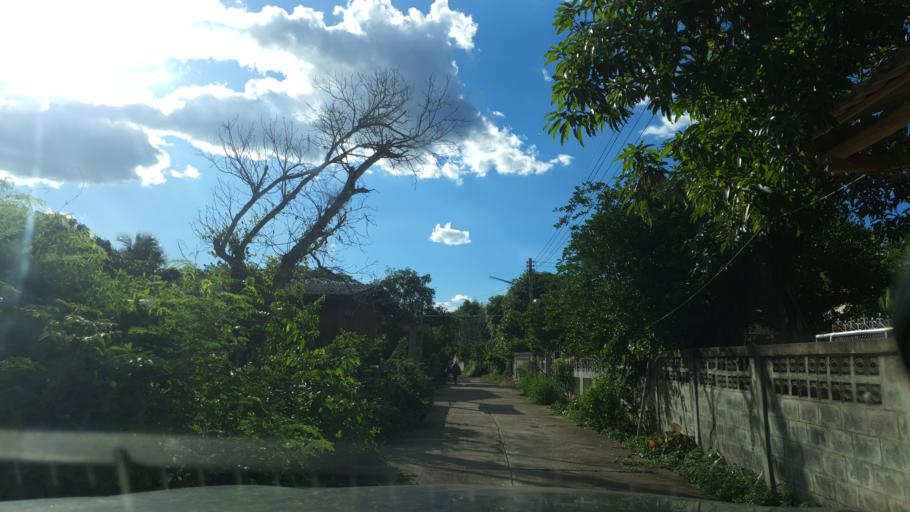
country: TH
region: Lampang
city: Sop Prap
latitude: 17.8797
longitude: 99.2961
